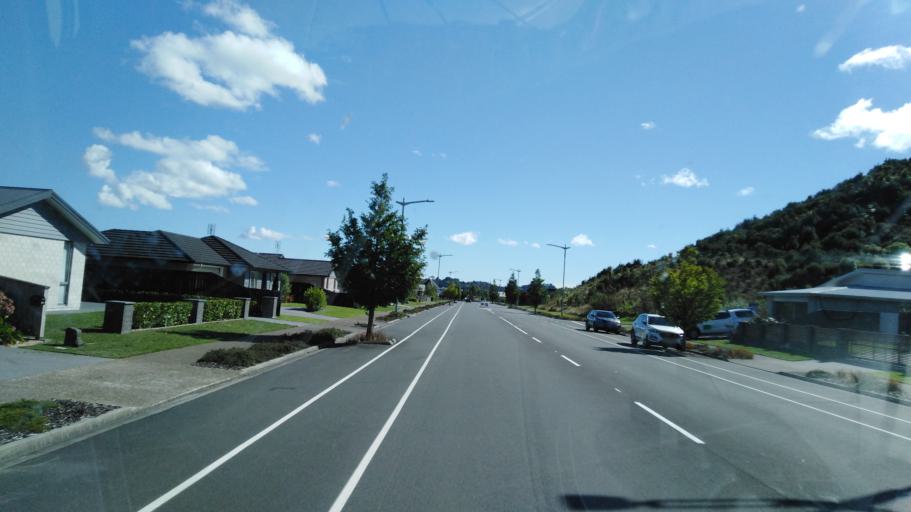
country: NZ
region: Bay of Plenty
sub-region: Tauranga City
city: Tauranga
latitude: -37.7589
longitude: 176.1038
